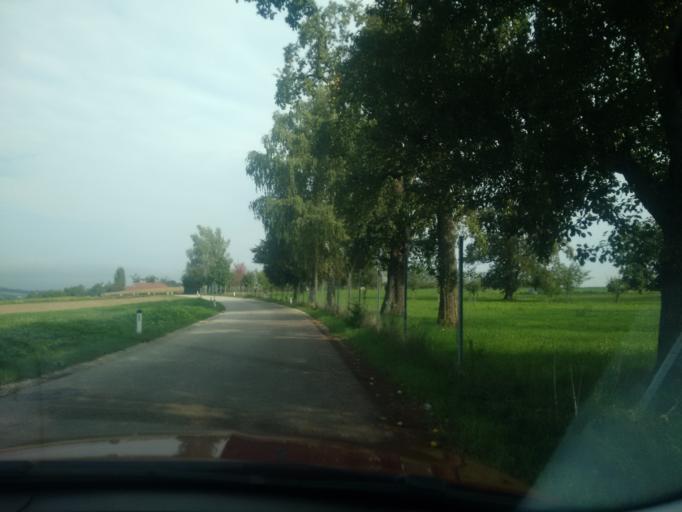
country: AT
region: Upper Austria
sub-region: Wels-Land
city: Steinhaus
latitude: 48.1069
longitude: 14.0273
